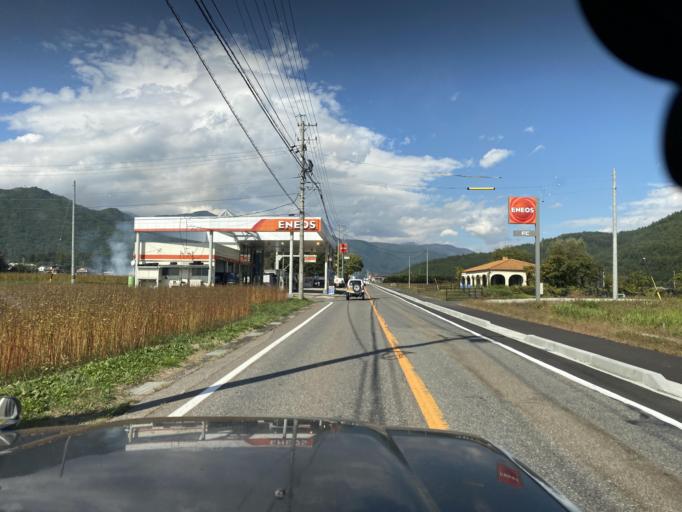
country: JP
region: Nagano
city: Omachi
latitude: 36.5296
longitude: 137.8484
